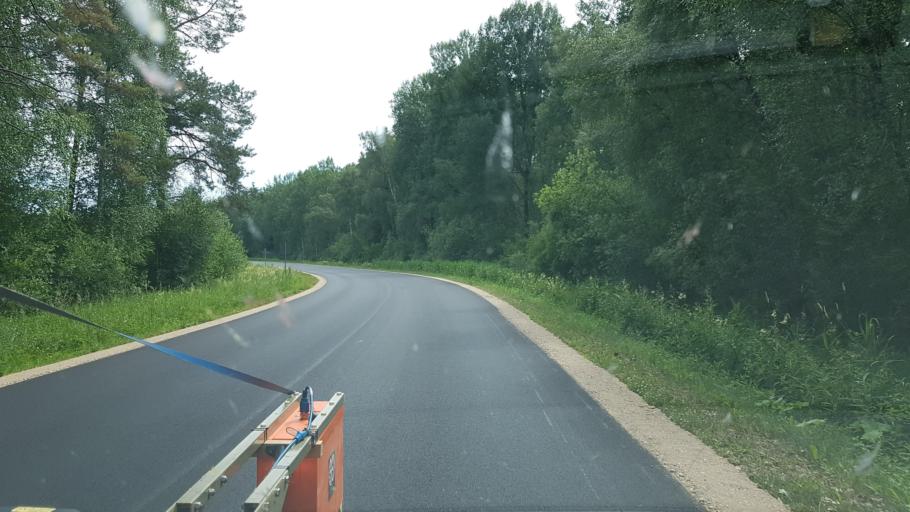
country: EE
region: Paernumaa
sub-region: Audru vald
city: Audru
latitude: 58.6234
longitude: 24.2489
